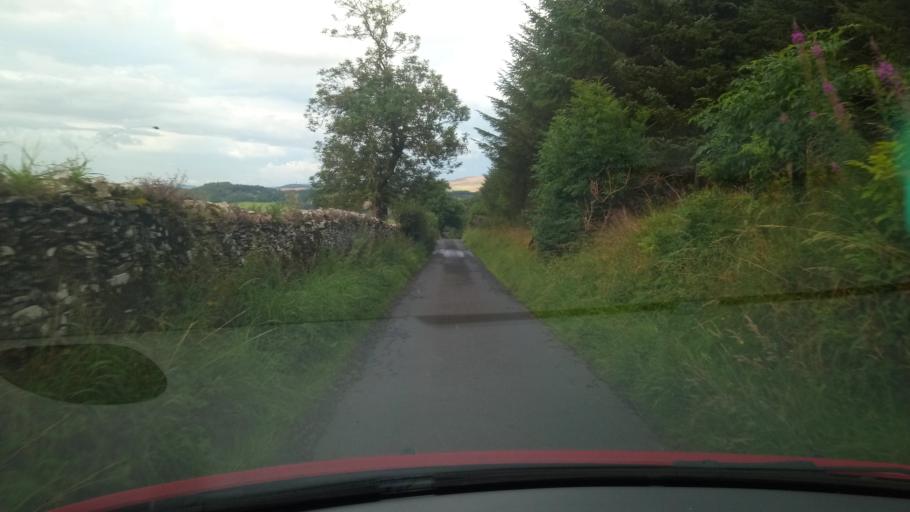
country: GB
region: Scotland
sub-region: The Scottish Borders
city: Hawick
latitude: 55.4170
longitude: -2.7620
